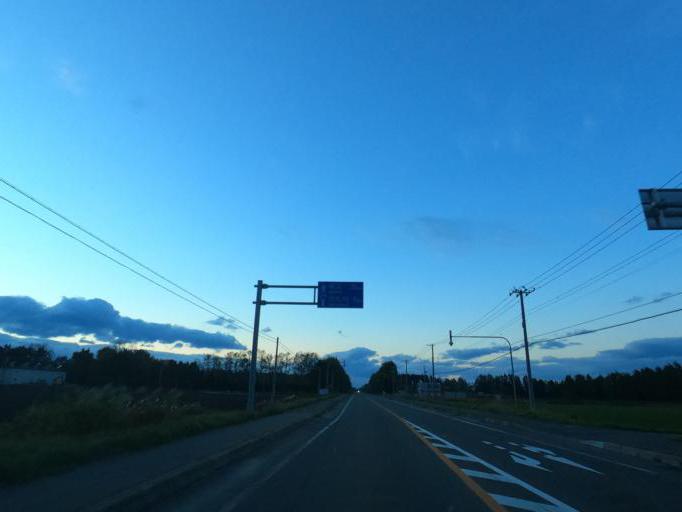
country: JP
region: Hokkaido
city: Obihiro
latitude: 42.6545
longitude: 143.1885
